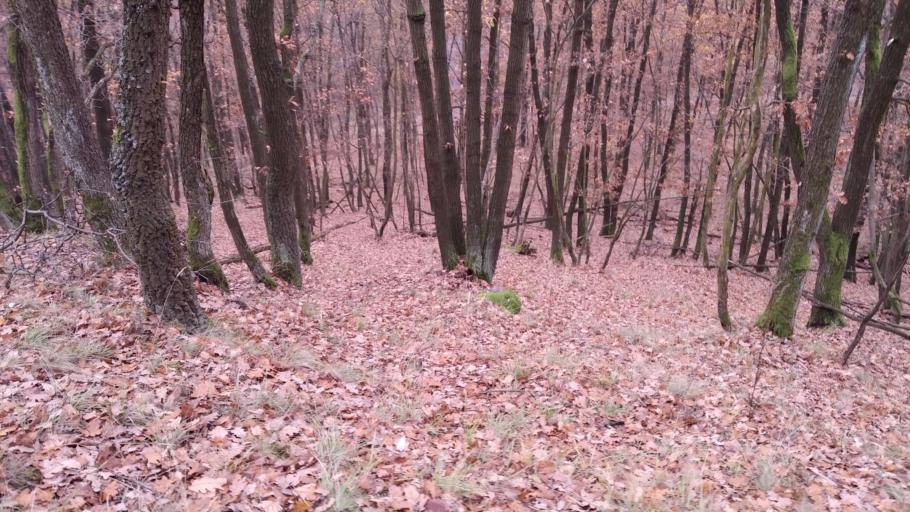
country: HU
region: Pest
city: Csobanka
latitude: 47.6811
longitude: 18.9548
